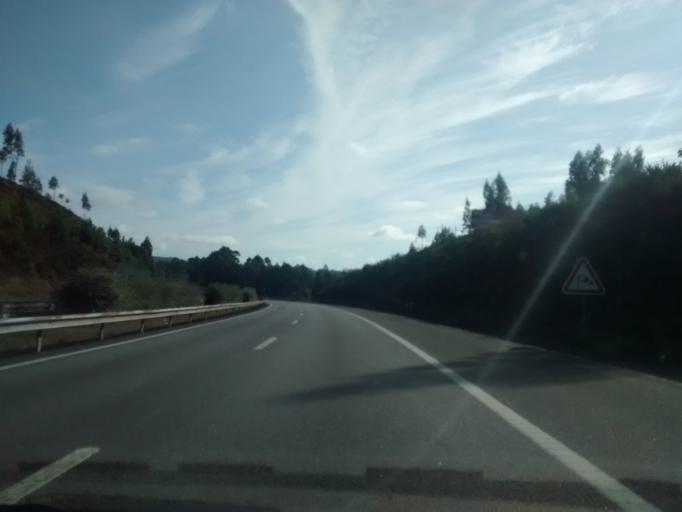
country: PT
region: Porto
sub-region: Santo Tirso
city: Santo Tirso
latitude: 41.3551
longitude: -8.5058
